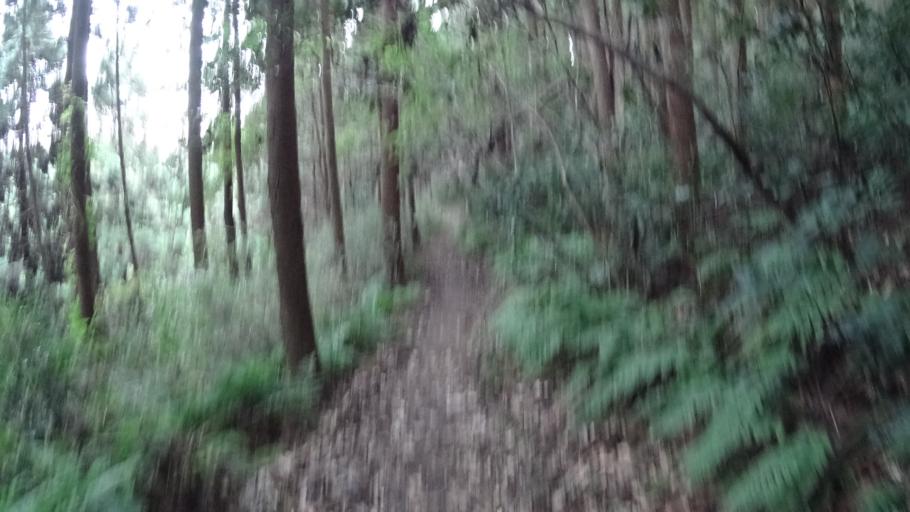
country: JP
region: Kanagawa
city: Zushi
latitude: 35.2860
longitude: 139.6211
